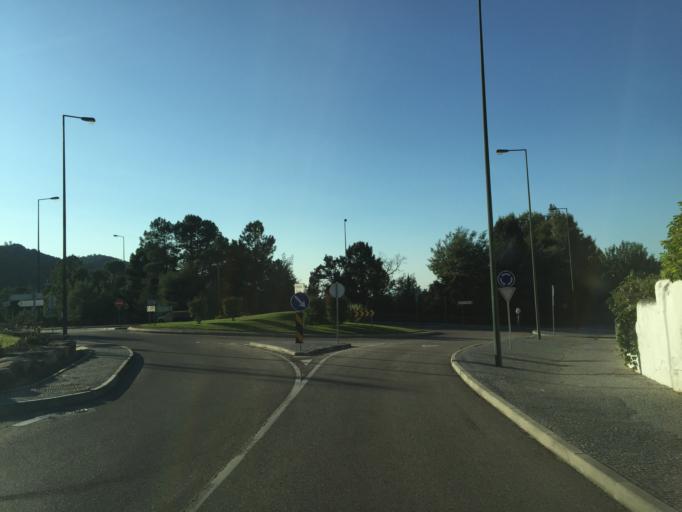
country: PT
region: Portalegre
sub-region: Castelo de Vide
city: Castelo de Vide
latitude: 39.4060
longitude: -7.4447
